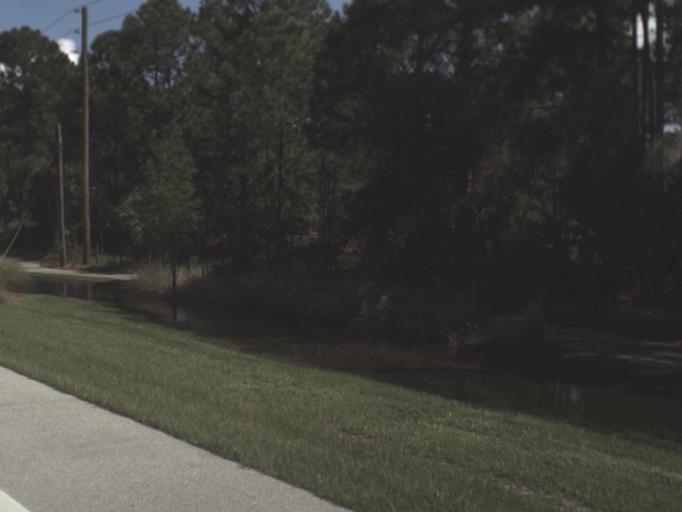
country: US
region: Florida
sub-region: Sarasota County
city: North Port
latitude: 27.0696
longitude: -82.1567
